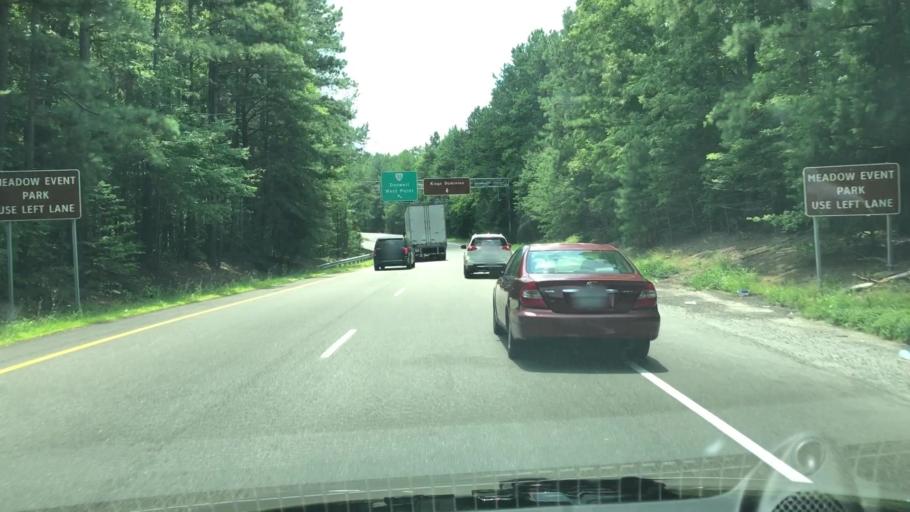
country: US
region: Virginia
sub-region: Hanover County
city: Ashland
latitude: 37.8474
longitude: -77.4548
